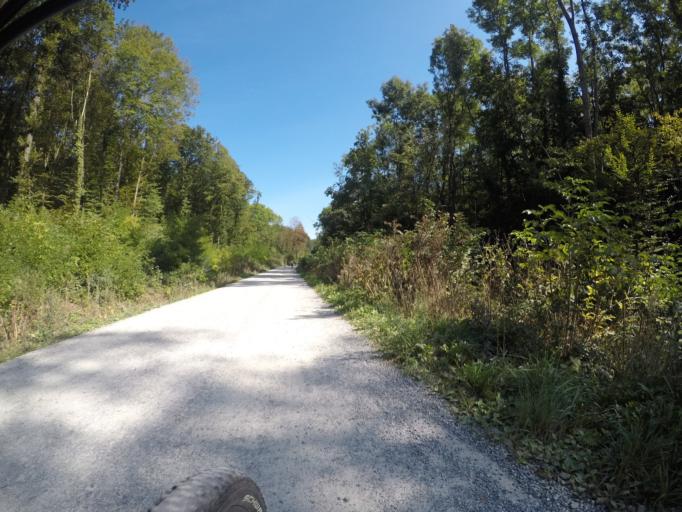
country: AT
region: Lower Austria
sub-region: Politischer Bezirk Bruck an der Leitha
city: Hof am Leithaberge
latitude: 47.9562
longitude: 16.5933
